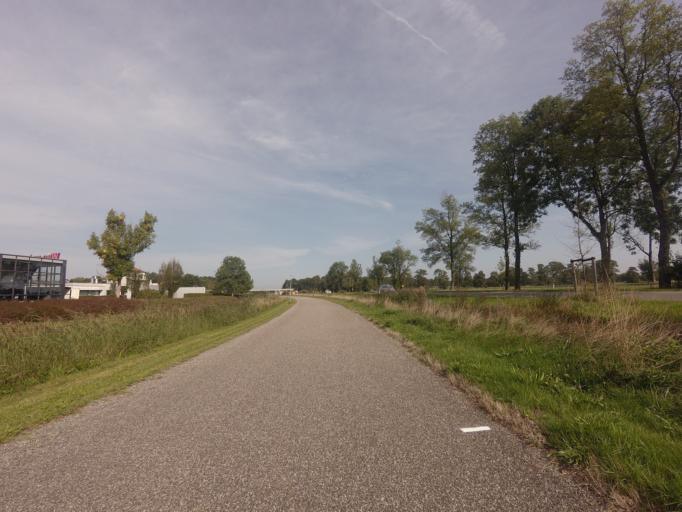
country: NL
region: Groningen
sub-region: Gemeente Leek
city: Leek
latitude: 53.1821
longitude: 6.3802
